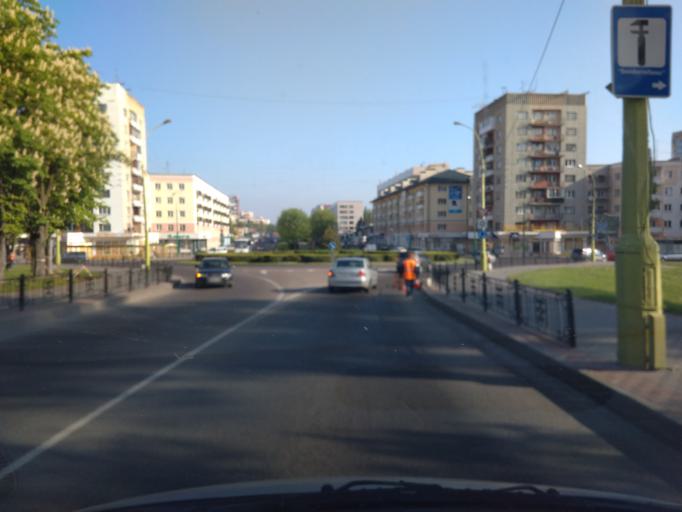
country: BY
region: Brest
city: Brest
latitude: 52.0833
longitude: 23.7048
